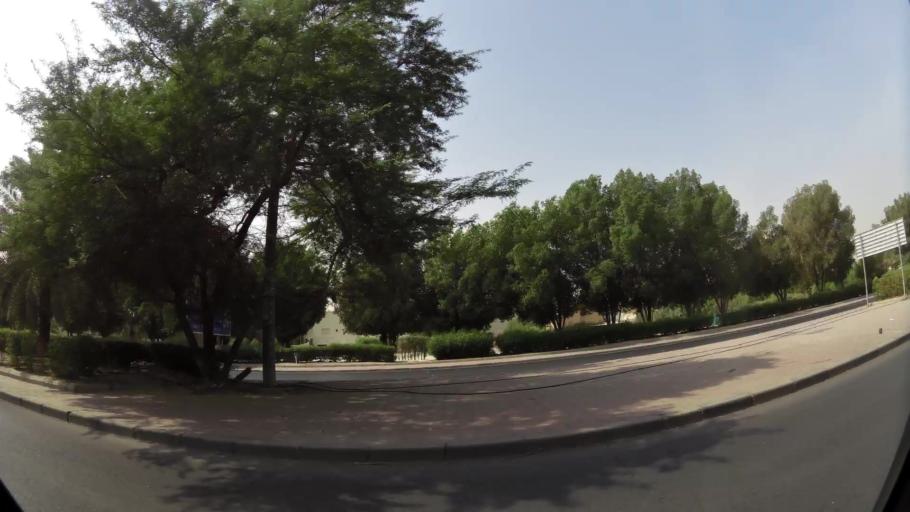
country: KW
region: Al Asimah
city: Ar Rabiyah
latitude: 29.2818
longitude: 47.9068
